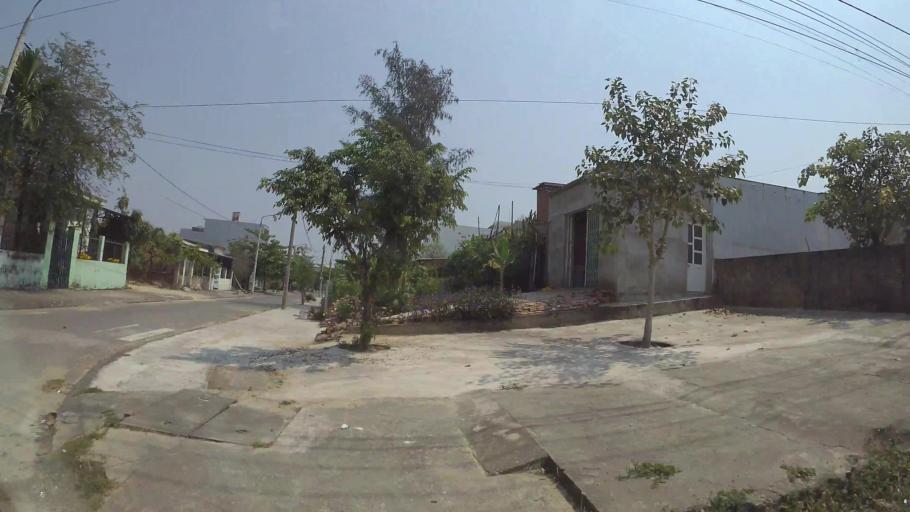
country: VN
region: Da Nang
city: Ngu Hanh Son
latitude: 16.0094
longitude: 108.2527
